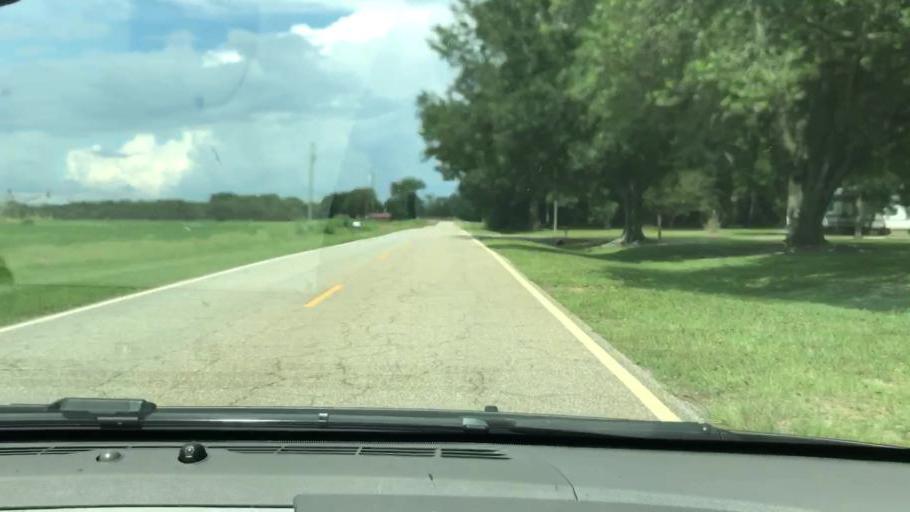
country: US
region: Georgia
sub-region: Early County
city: Blakely
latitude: 31.2272
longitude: -84.9951
